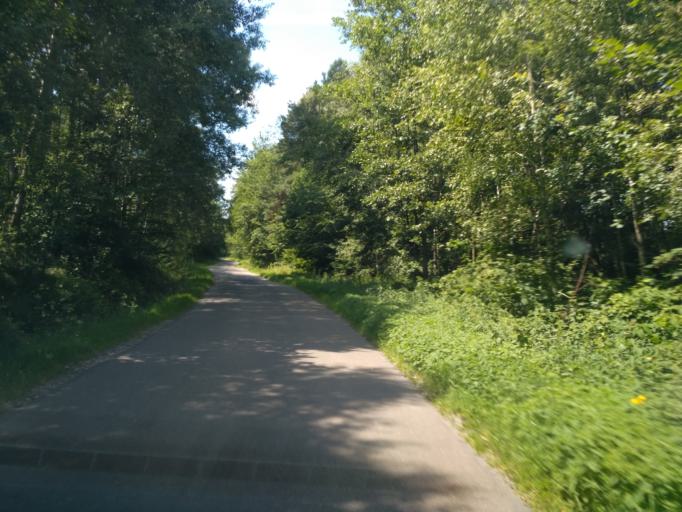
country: PL
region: Subcarpathian Voivodeship
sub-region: Powiat strzyzowski
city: Jawornik
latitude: 49.8578
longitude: 21.8881
